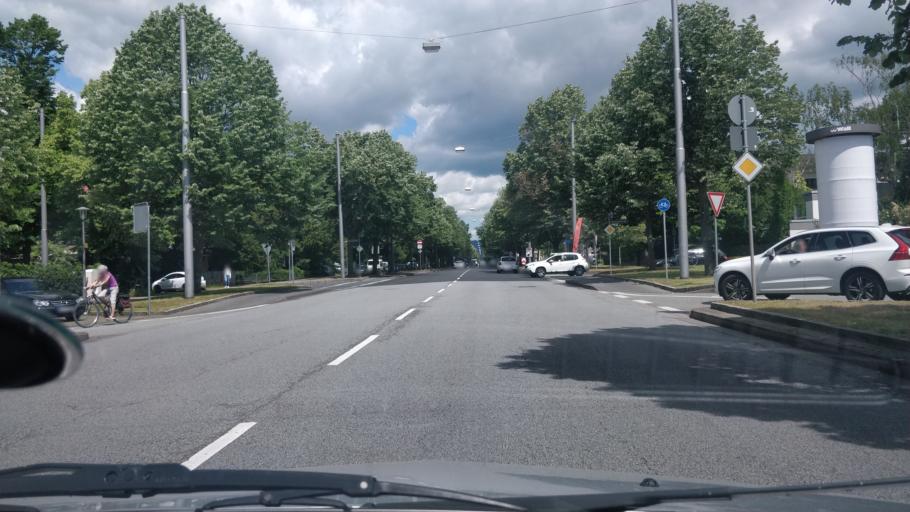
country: DE
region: Hesse
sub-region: Regierungsbezirk Darmstadt
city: Wiesbaden
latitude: 50.0562
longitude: 8.2436
